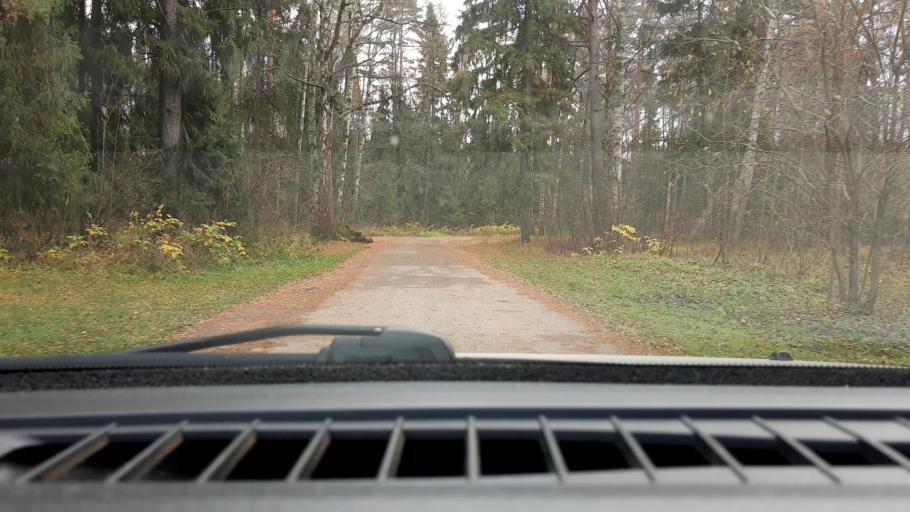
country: RU
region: Nizjnij Novgorod
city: Kstovo
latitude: 56.1709
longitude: 44.1329
